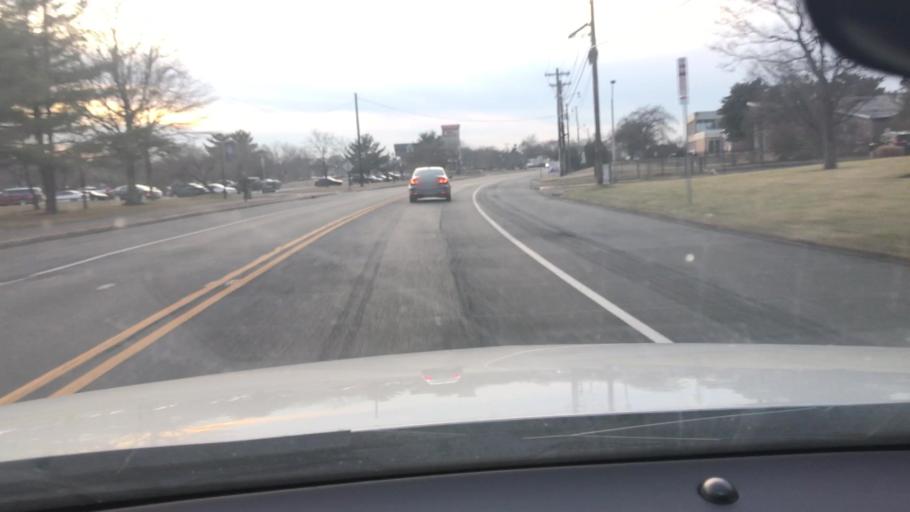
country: US
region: New Jersey
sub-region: Camden County
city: Collingswood
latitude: 39.9275
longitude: -75.0685
